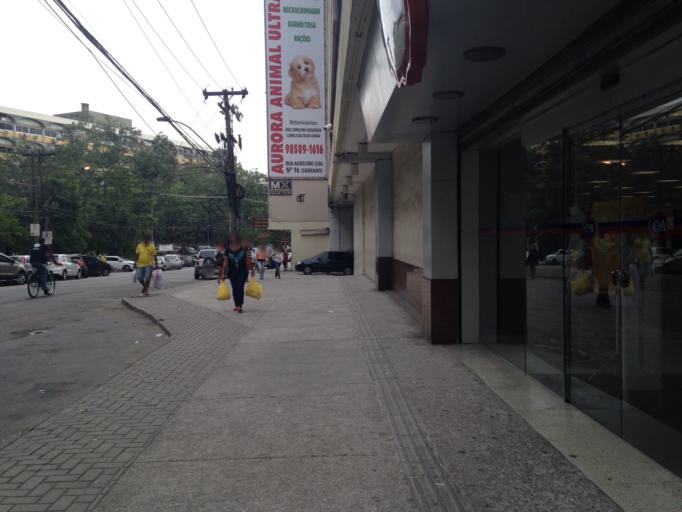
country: BR
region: Rio de Janeiro
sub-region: Niteroi
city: Niteroi
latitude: -22.8975
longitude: -43.1243
